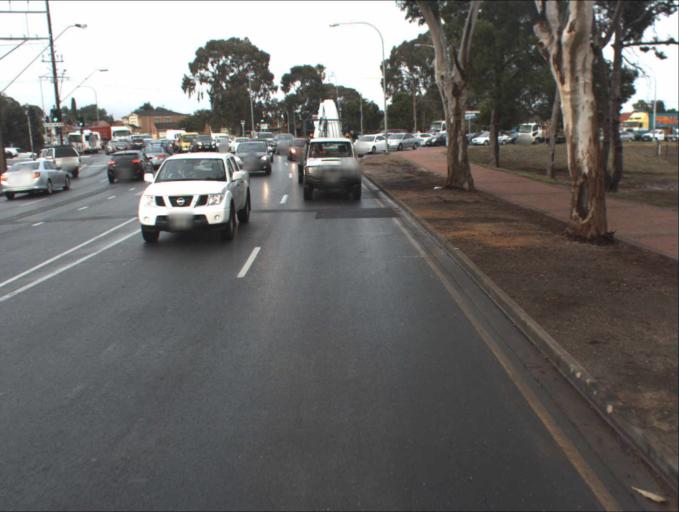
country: AU
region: South Australia
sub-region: Port Adelaide Enfield
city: Enfield
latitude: -34.8466
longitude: 138.6177
